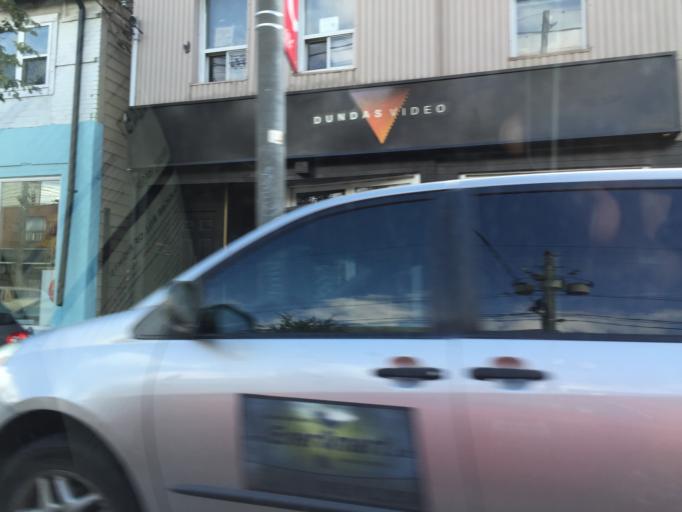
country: CA
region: Ontario
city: Toronto
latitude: 43.6516
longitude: -79.4094
